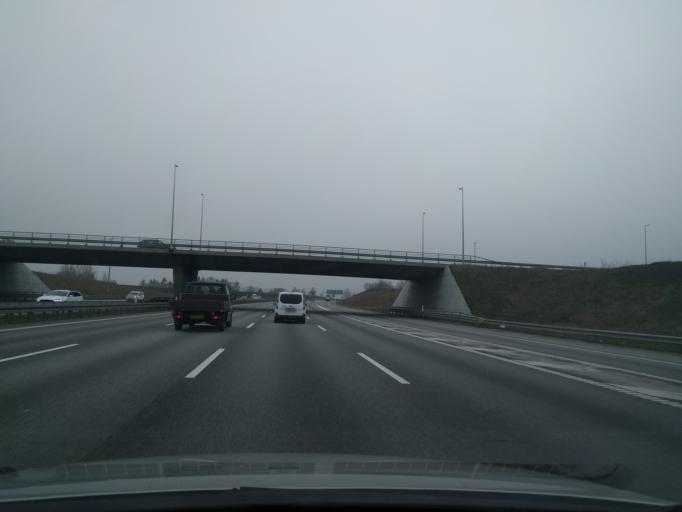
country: DK
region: Zealand
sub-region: Koge Kommune
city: Koge
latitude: 55.4903
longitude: 12.1626
